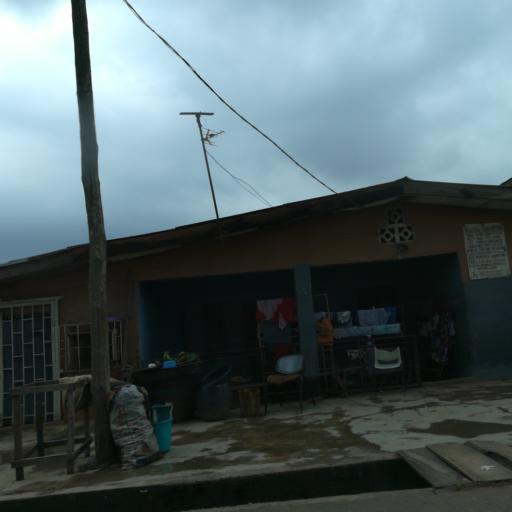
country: NG
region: Lagos
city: Agege
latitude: 6.6083
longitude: 3.3066
